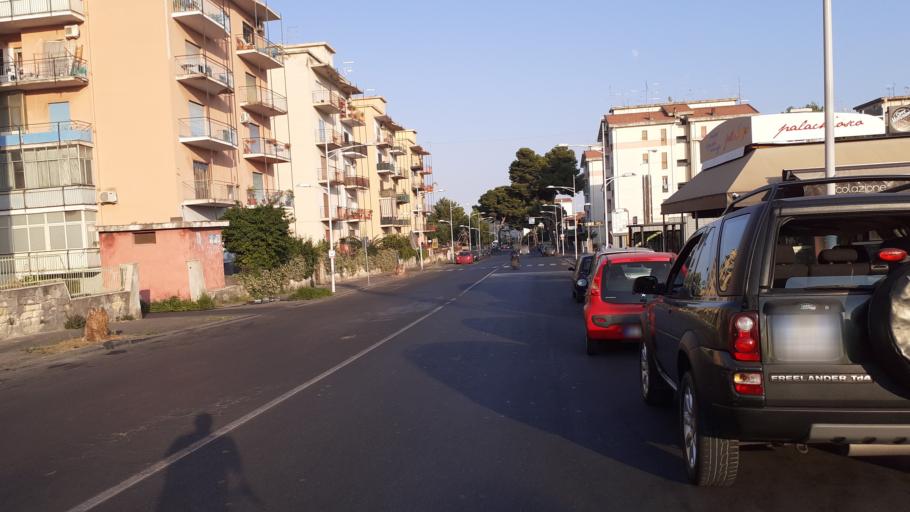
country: IT
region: Sicily
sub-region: Catania
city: Catania
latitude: 37.5040
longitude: 15.0564
